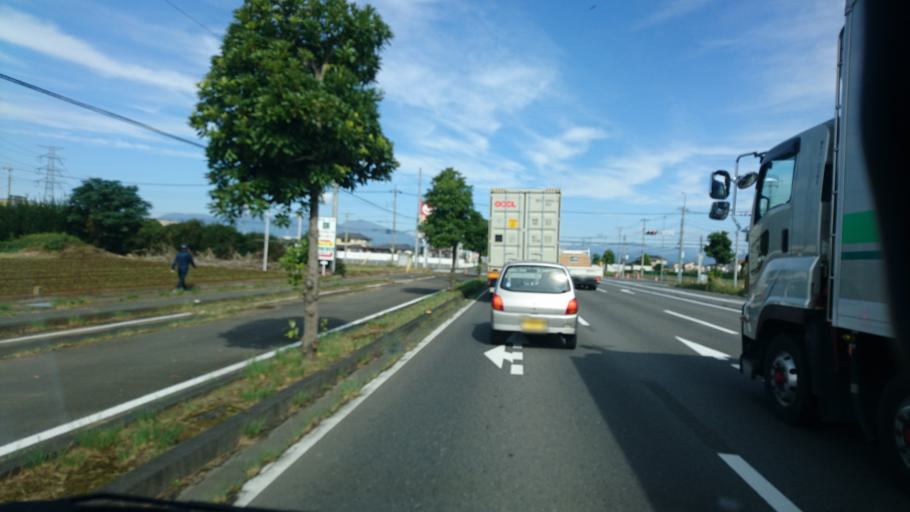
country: JP
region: Gunma
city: Kiryu
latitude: 36.3569
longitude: 139.2804
